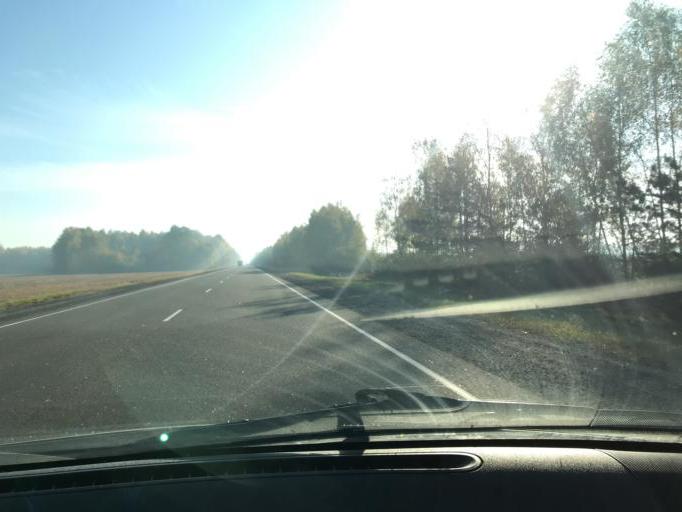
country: BY
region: Brest
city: Horad Luninyets
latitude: 52.3039
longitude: 26.7051
